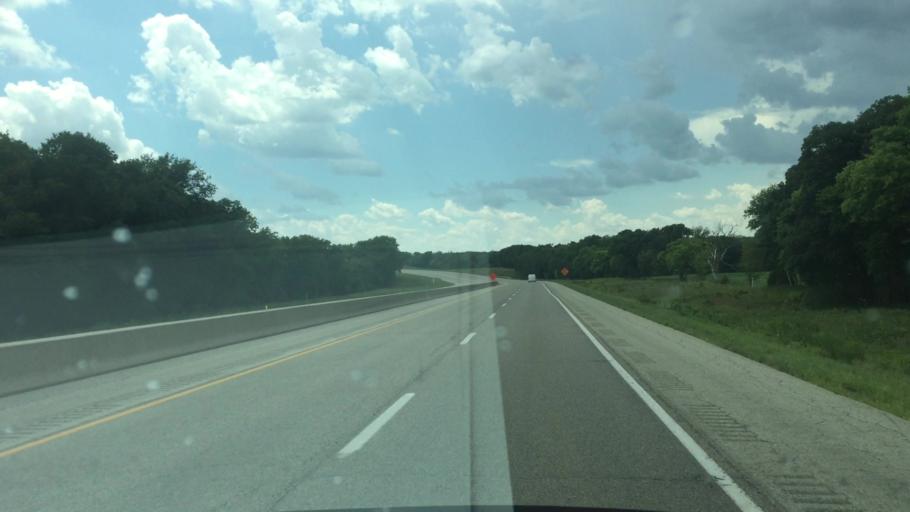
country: US
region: Kansas
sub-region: Shawnee County
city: Auburn
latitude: 38.9292
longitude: -95.7652
